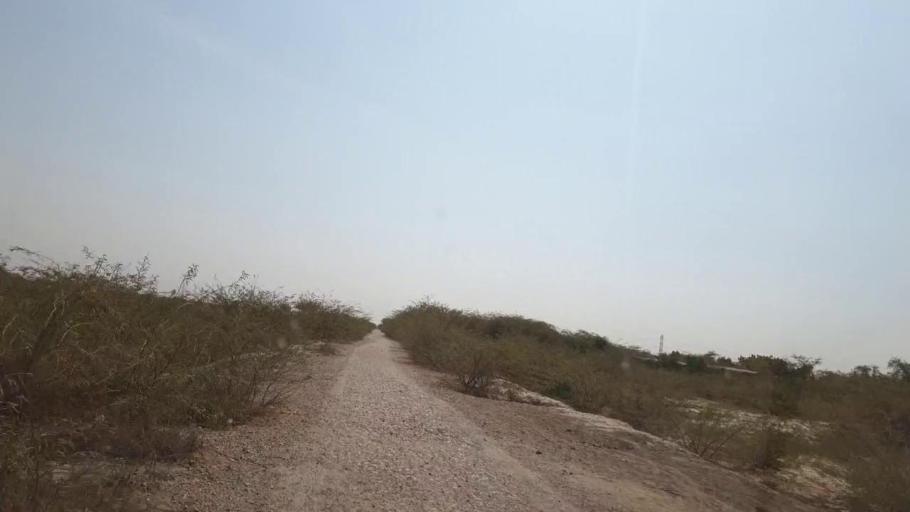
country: PK
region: Sindh
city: Nabisar
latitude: 25.0628
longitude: 69.5526
